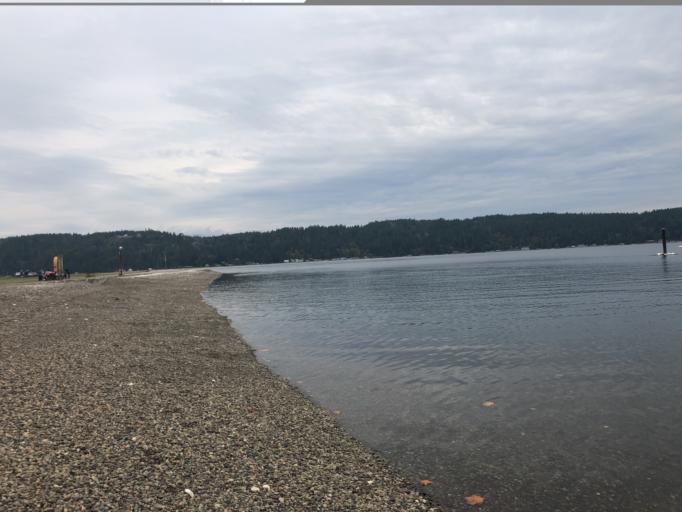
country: US
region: Washington
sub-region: Mason County
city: Allyn
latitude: 47.3789
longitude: -122.9714
